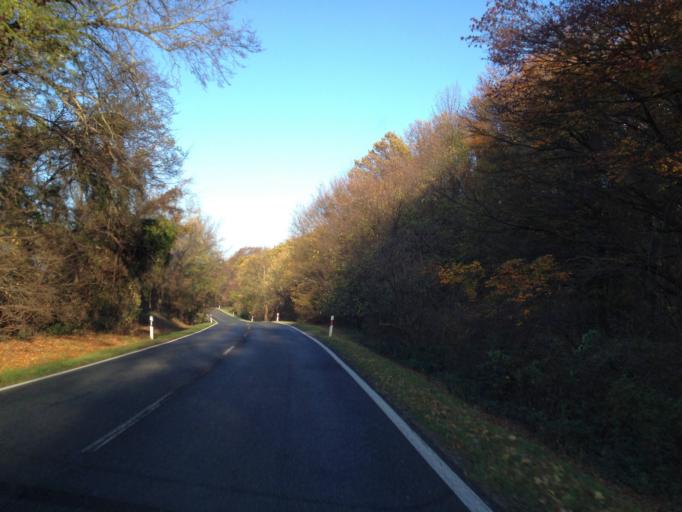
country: HU
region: Veszprem
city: Zirc
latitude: 47.3304
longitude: 17.8802
